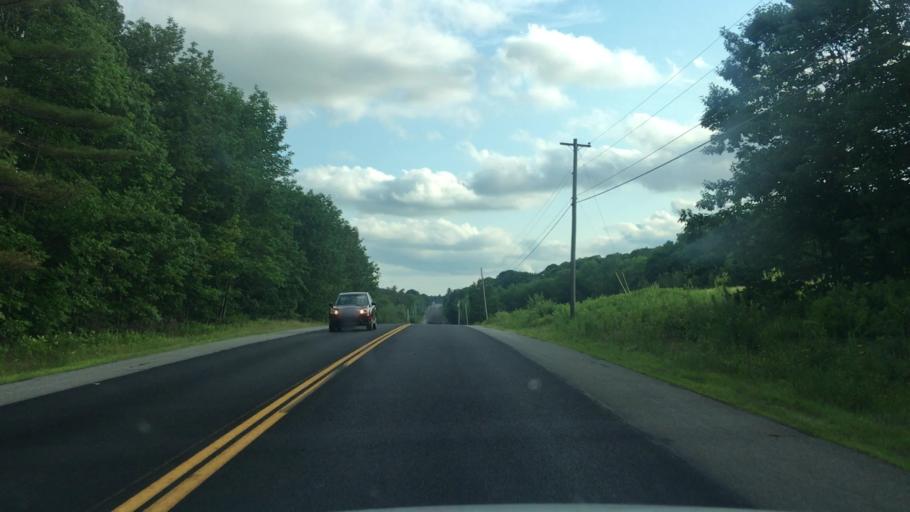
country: US
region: Maine
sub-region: Knox County
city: Washington
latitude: 44.3965
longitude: -69.3496
